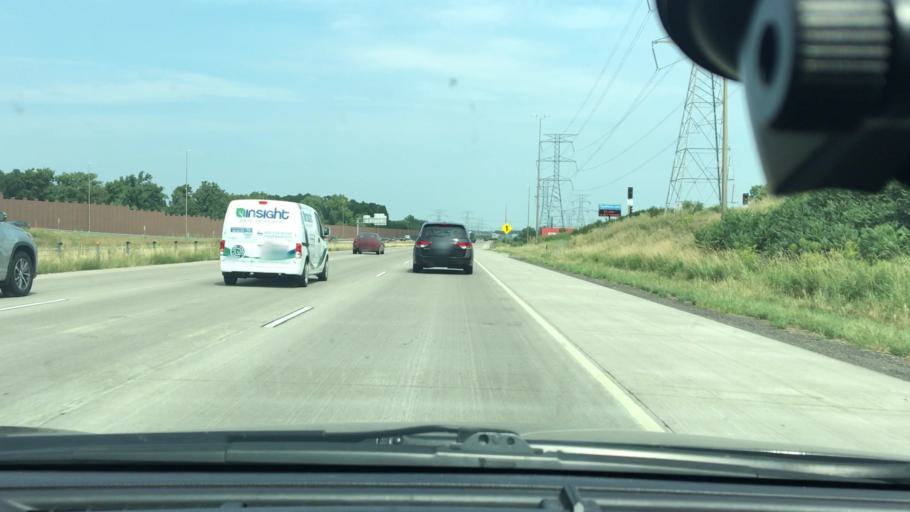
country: US
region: Minnesota
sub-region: Hennepin County
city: Plymouth
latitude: 44.9849
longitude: -93.4596
